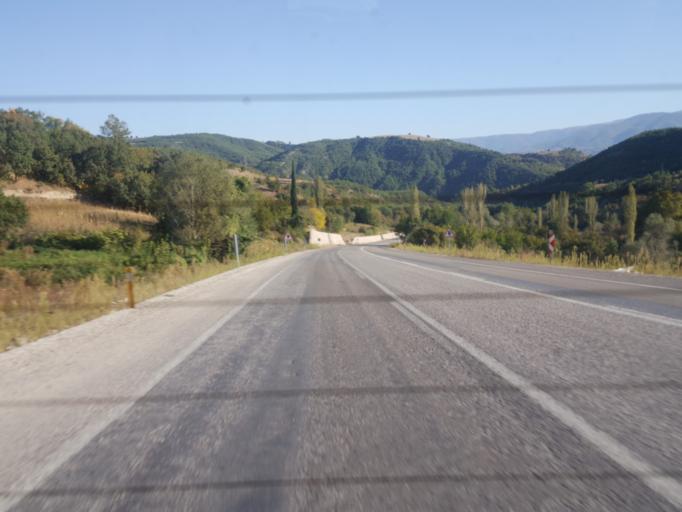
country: TR
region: Amasya
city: Tasova
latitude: 40.7604
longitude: 36.2841
